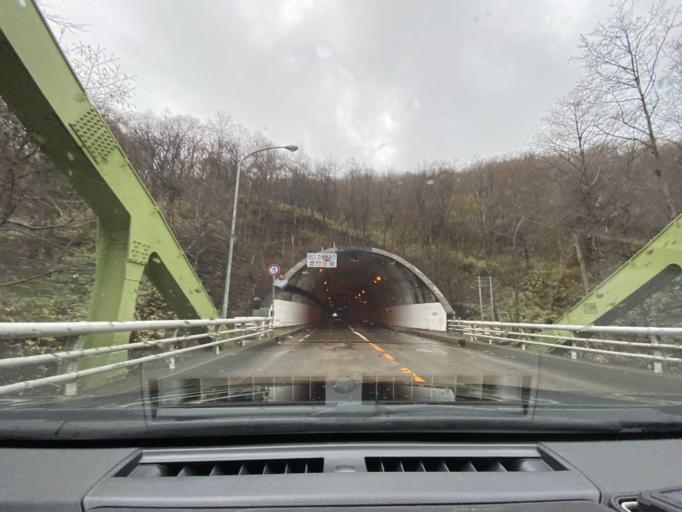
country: JP
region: Hokkaido
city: Rumoi
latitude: 43.8210
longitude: 141.4323
